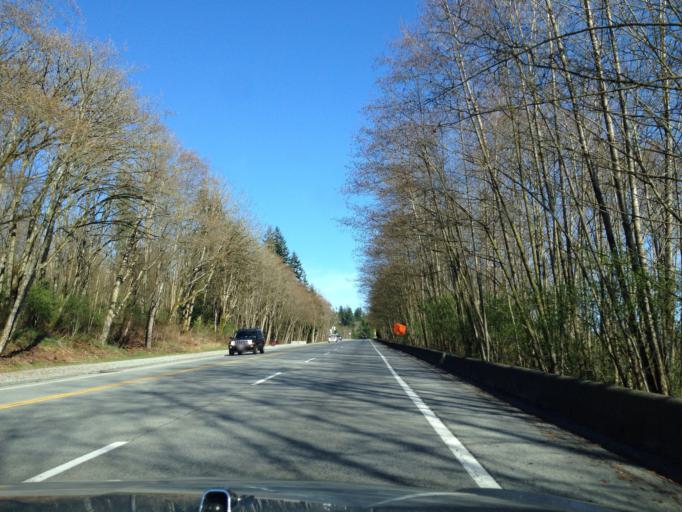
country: CA
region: British Columbia
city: Burnaby
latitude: 49.2738
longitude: -122.9331
